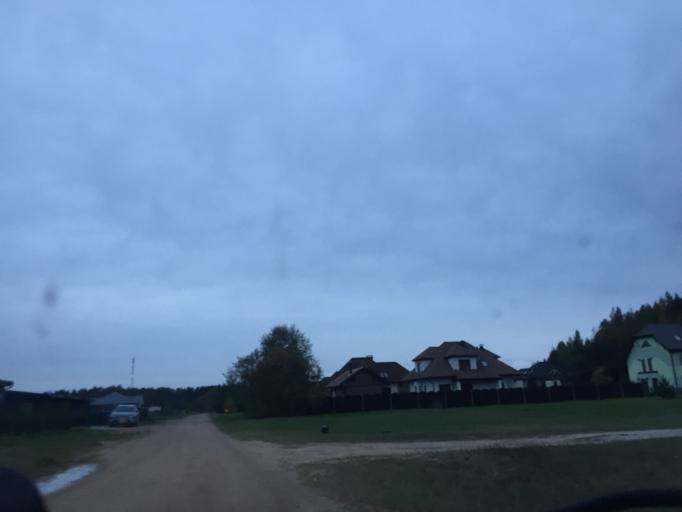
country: LV
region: Adazi
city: Adazi
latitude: 57.0855
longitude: 24.3768
